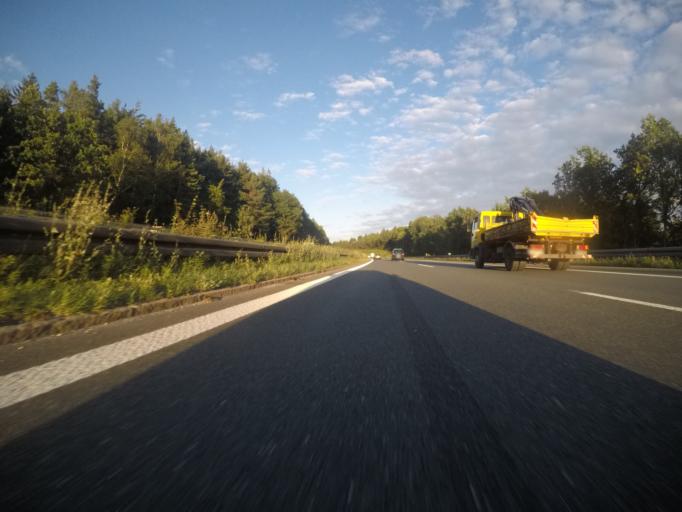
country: DE
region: Bavaria
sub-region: Regierungsbezirk Mittelfranken
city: Altdorf
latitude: 49.4010
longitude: 11.3752
